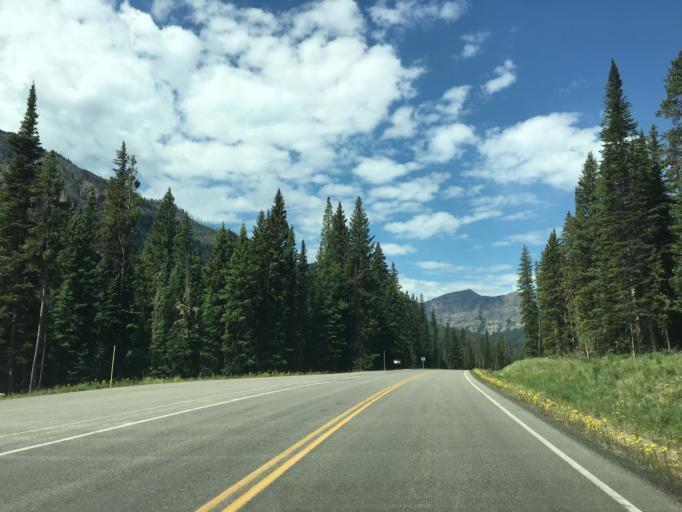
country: US
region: Montana
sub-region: Stillwater County
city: Absarokee
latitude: 45.0040
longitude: -109.9964
